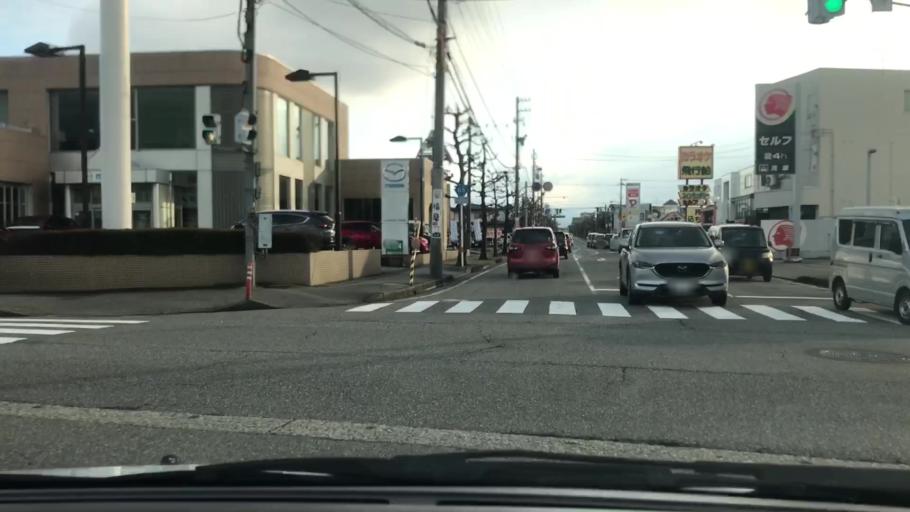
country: JP
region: Toyama
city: Toyama-shi
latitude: 36.6775
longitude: 137.2370
